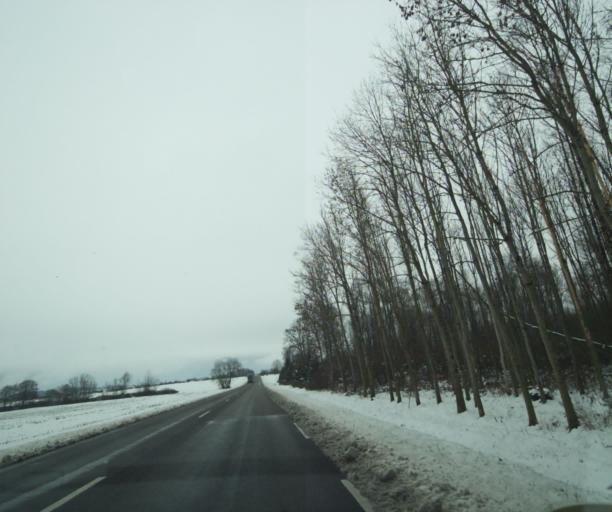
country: FR
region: Champagne-Ardenne
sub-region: Departement de la Haute-Marne
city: Montier-en-Der
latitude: 48.4315
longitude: 4.6995
